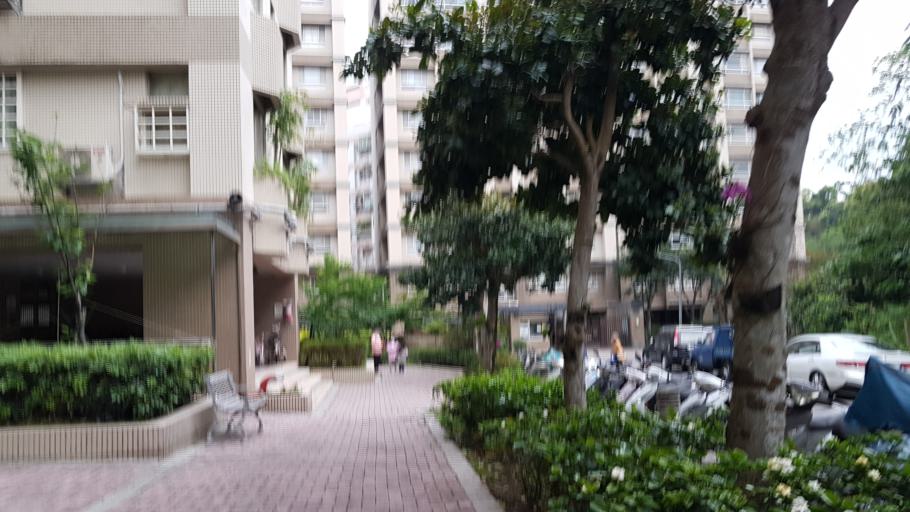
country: TW
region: Taipei
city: Taipei
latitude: 25.0049
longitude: 121.5482
